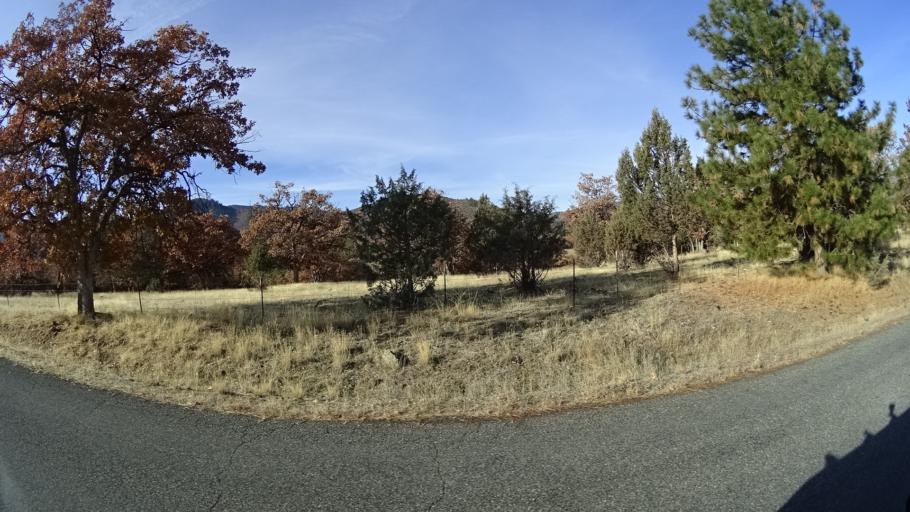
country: US
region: California
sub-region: Siskiyou County
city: Yreka
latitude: 41.6700
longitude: -122.6232
